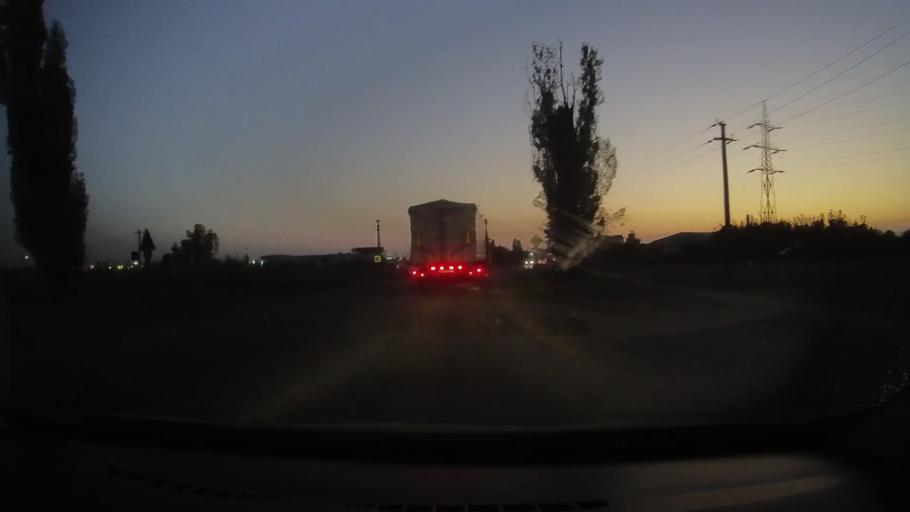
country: RO
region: Arad
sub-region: Comuna Vladimirescu
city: Vladimirescu
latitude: 46.1787
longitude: 21.3720
